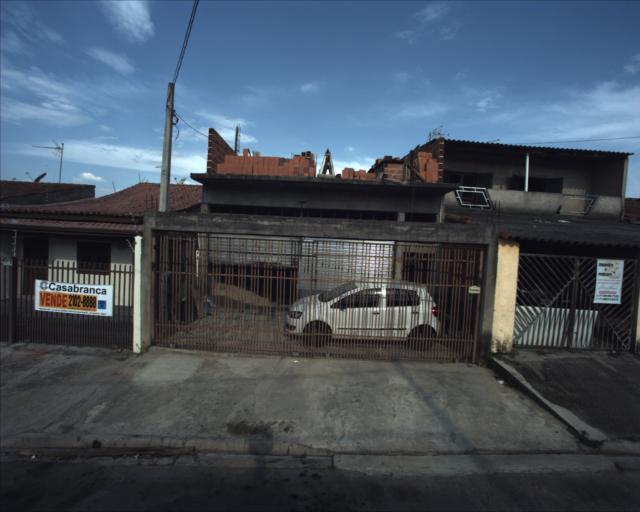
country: BR
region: Sao Paulo
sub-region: Sorocaba
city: Sorocaba
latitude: -23.4982
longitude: -47.5229
